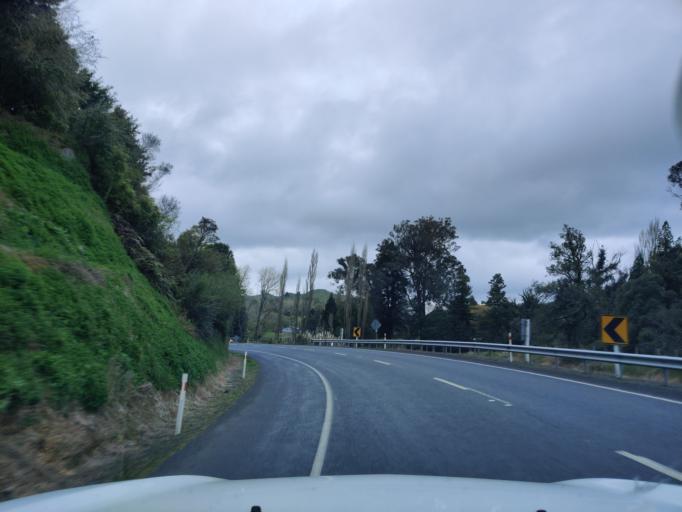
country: NZ
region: Waikato
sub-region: Otorohanga District
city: Otorohanga
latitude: -38.6077
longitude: 175.2171
